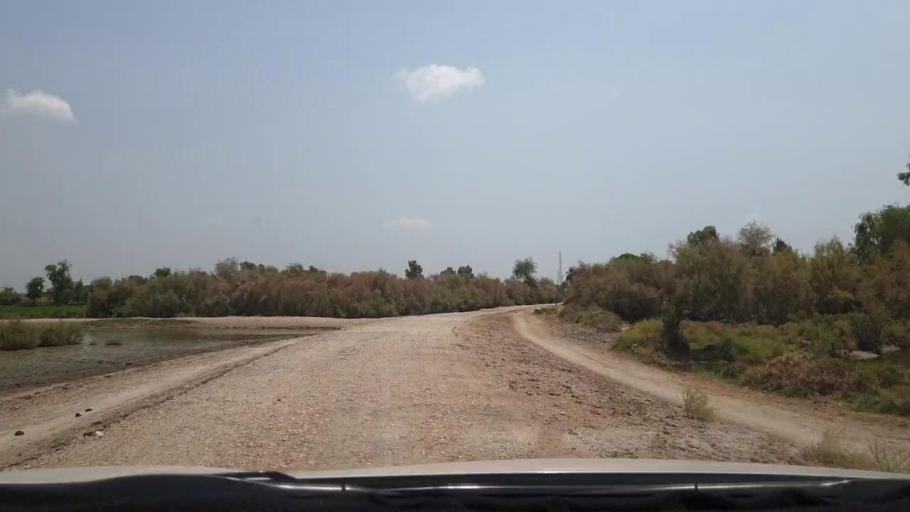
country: PK
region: Sindh
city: New Badah
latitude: 27.2979
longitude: 68.0676
